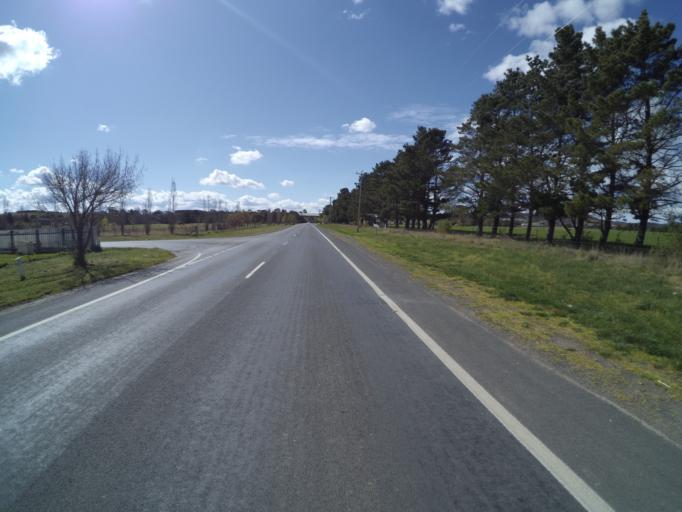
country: AU
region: New South Wales
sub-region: Goulburn Mulwaree
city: Goulburn
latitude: -34.7791
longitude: 149.7083
